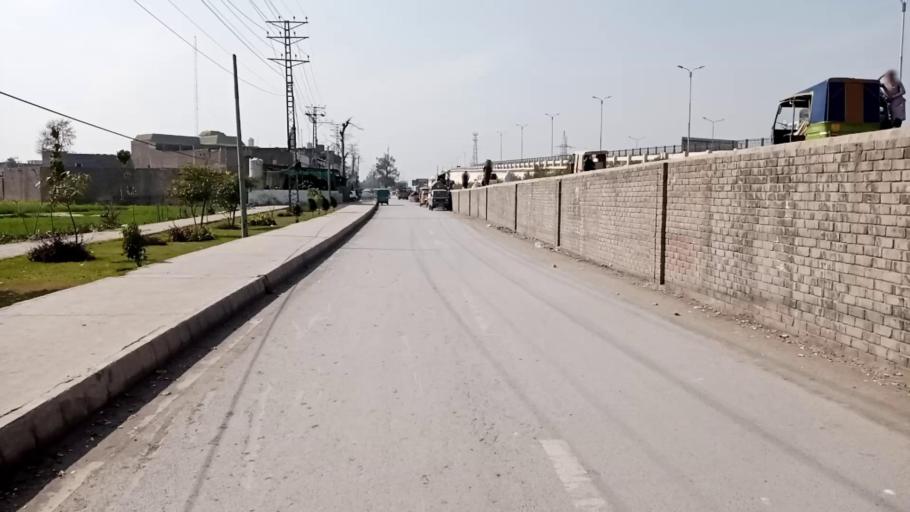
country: PK
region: Khyber Pakhtunkhwa
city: Peshawar
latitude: 34.0169
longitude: 71.6249
